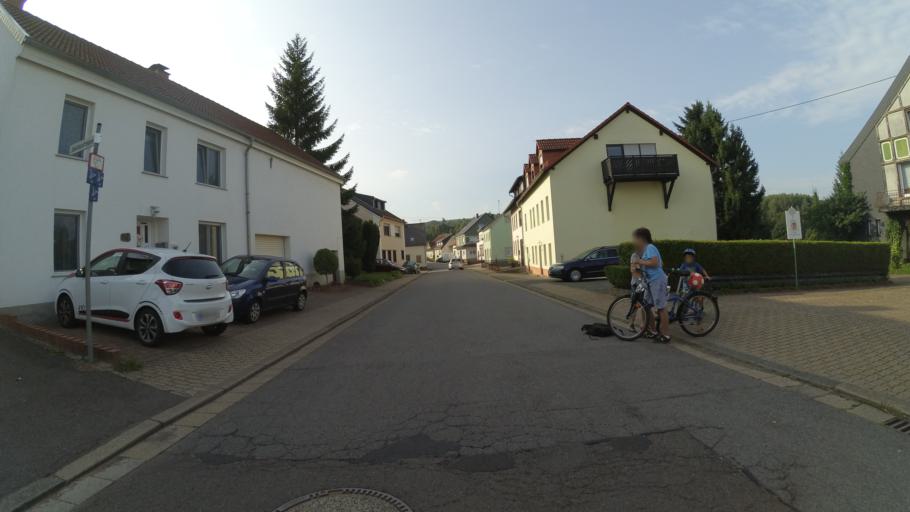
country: DE
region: Saarland
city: Weiskirchen
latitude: 49.5573
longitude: 6.8185
